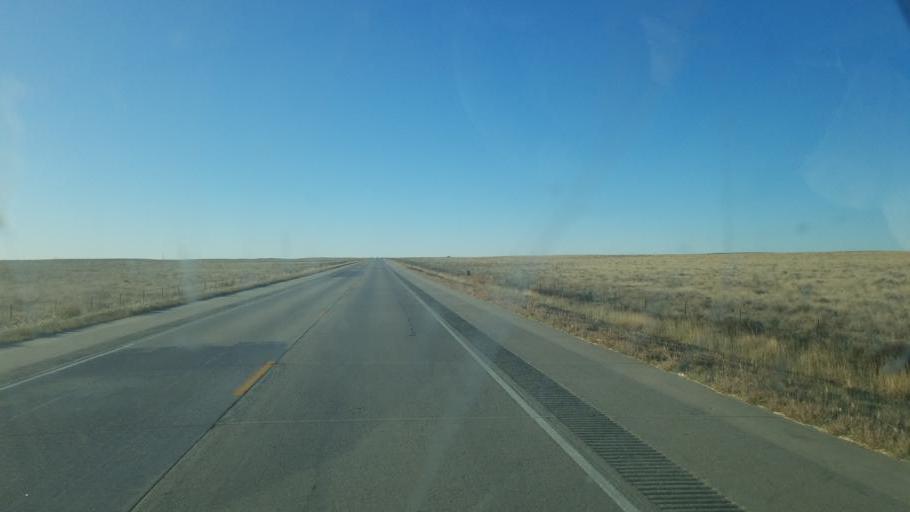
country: US
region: Colorado
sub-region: Kiowa County
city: Eads
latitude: 38.5647
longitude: -102.7862
